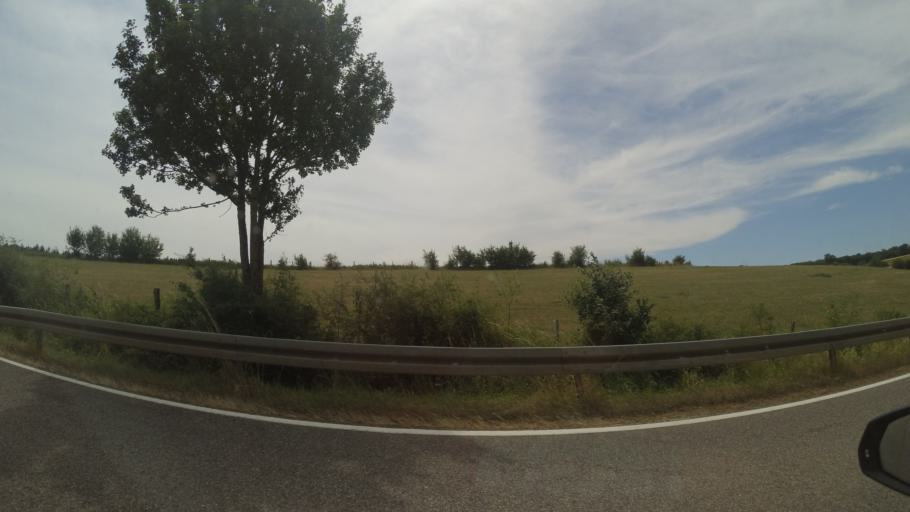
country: DE
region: Saarland
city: Mettlach
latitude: 49.4249
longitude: 6.5619
